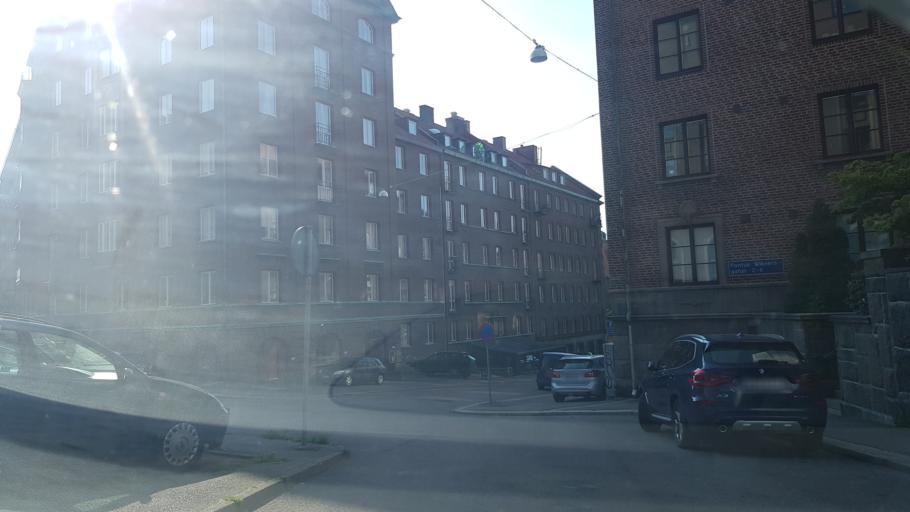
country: SE
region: Vaestra Goetaland
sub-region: Goteborg
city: Goeteborg
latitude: 57.6938
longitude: 11.9788
